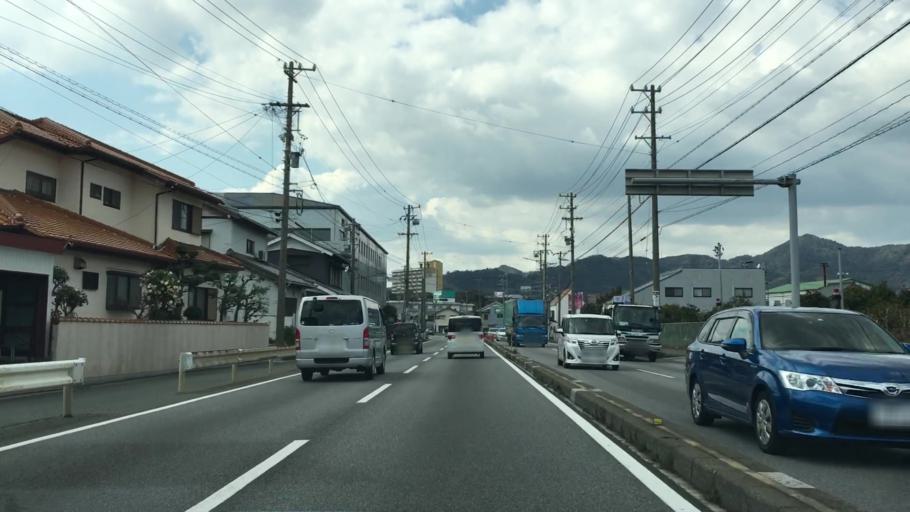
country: JP
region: Aichi
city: Kozakai-cho
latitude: 34.8102
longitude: 137.3031
